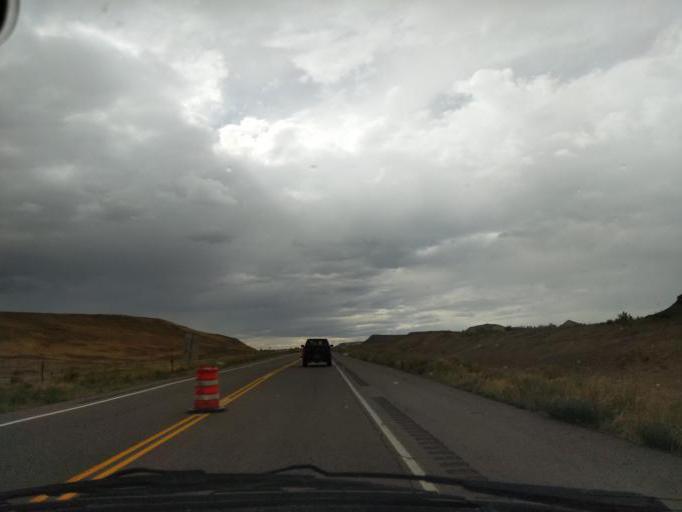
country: US
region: Colorado
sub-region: Delta County
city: Delta
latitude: 38.7532
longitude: -108.1680
